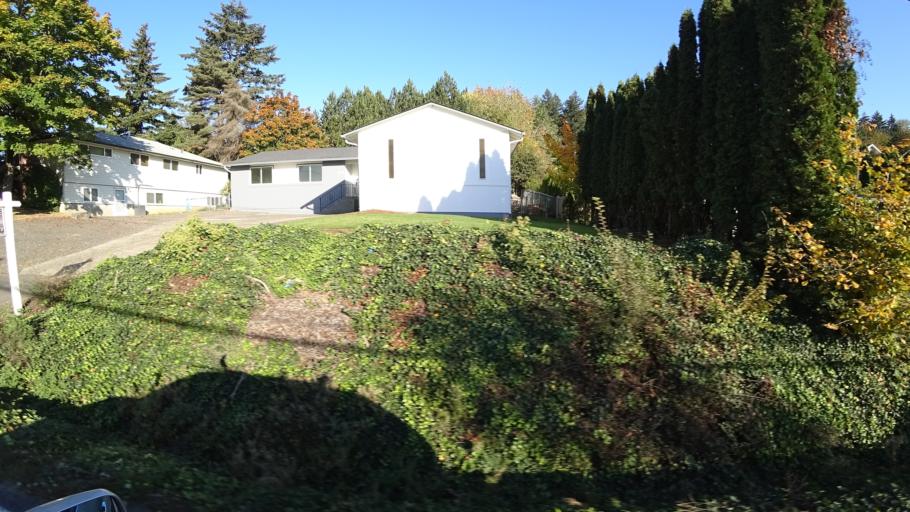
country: US
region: Oregon
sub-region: Multnomah County
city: Gresham
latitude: 45.4773
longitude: -122.4483
